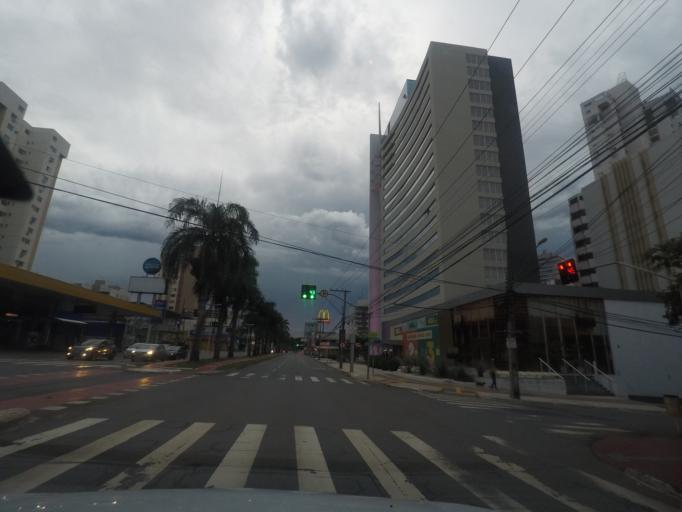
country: BR
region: Goias
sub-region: Goiania
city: Goiania
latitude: -16.7141
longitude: -49.2703
